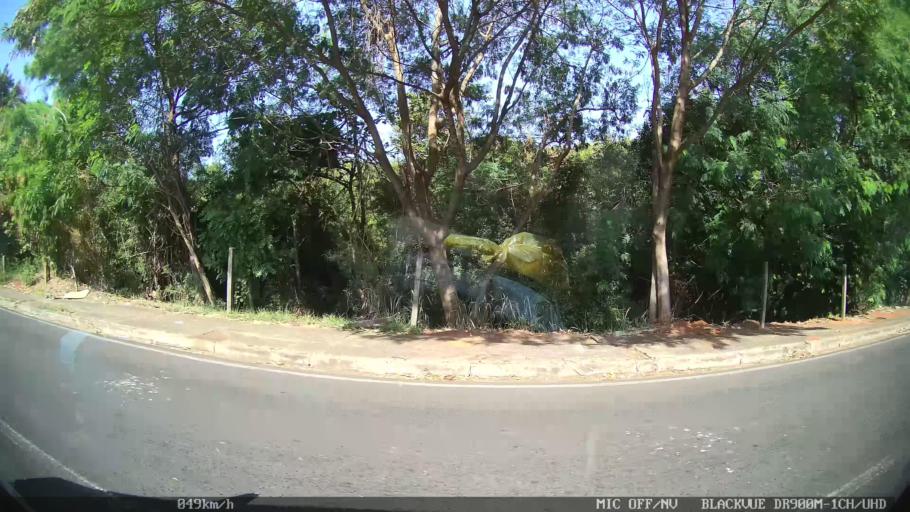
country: BR
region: Sao Paulo
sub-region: Sao Jose Do Rio Preto
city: Sao Jose do Rio Preto
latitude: -20.7935
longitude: -49.3947
